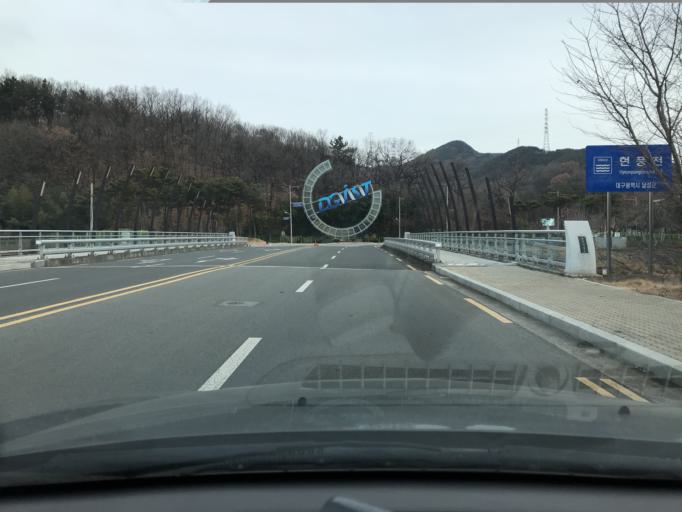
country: KR
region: Daegu
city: Hwawon
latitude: 35.6994
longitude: 128.4578
